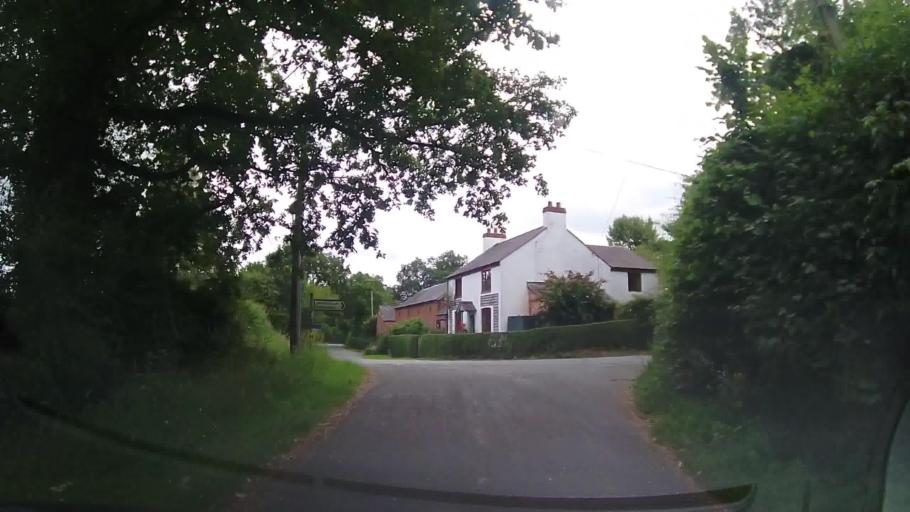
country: GB
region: England
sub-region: Shropshire
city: Prees
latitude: 52.9056
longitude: -2.7062
